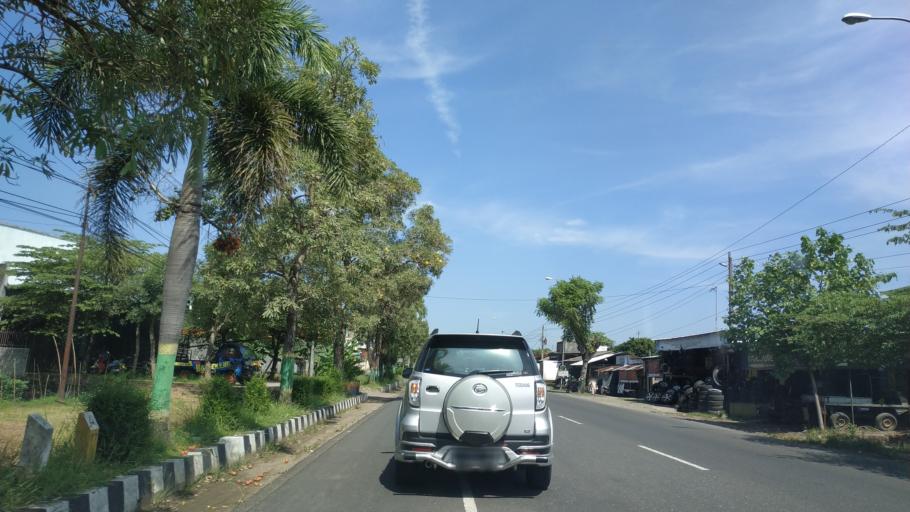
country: ID
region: Central Java
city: Geritan
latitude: -6.7501
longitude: 111.0574
